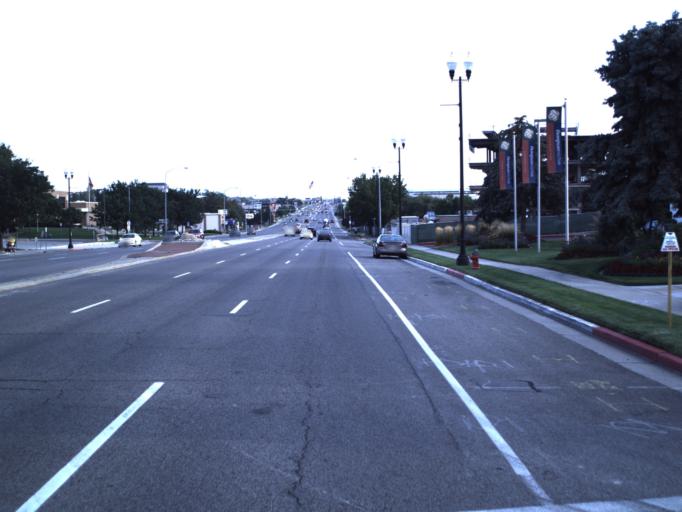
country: US
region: Utah
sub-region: Salt Lake County
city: Murray
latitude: 40.6643
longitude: -111.8884
